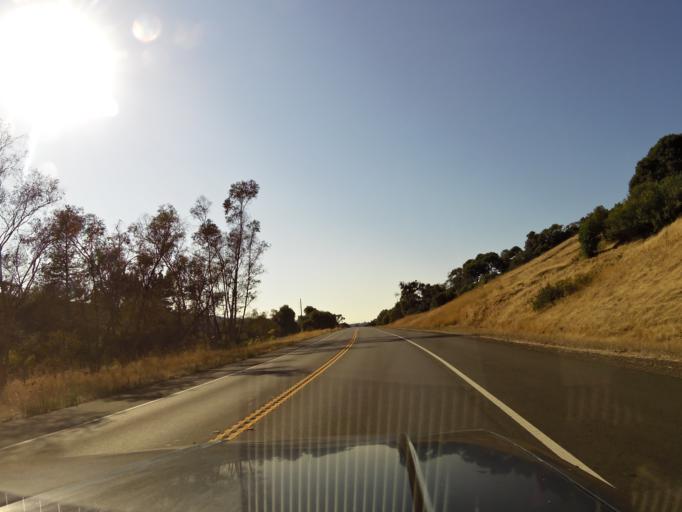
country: US
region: California
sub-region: Mendocino County
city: Boonville
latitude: 39.0364
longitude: -123.3929
